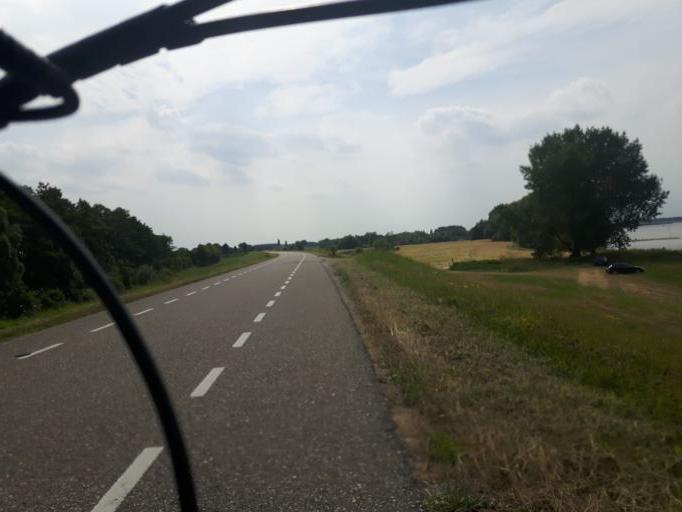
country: NL
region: Gelderland
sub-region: Gemeente Zaltbommel
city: Zaltbommel
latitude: 51.8103
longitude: 5.2297
